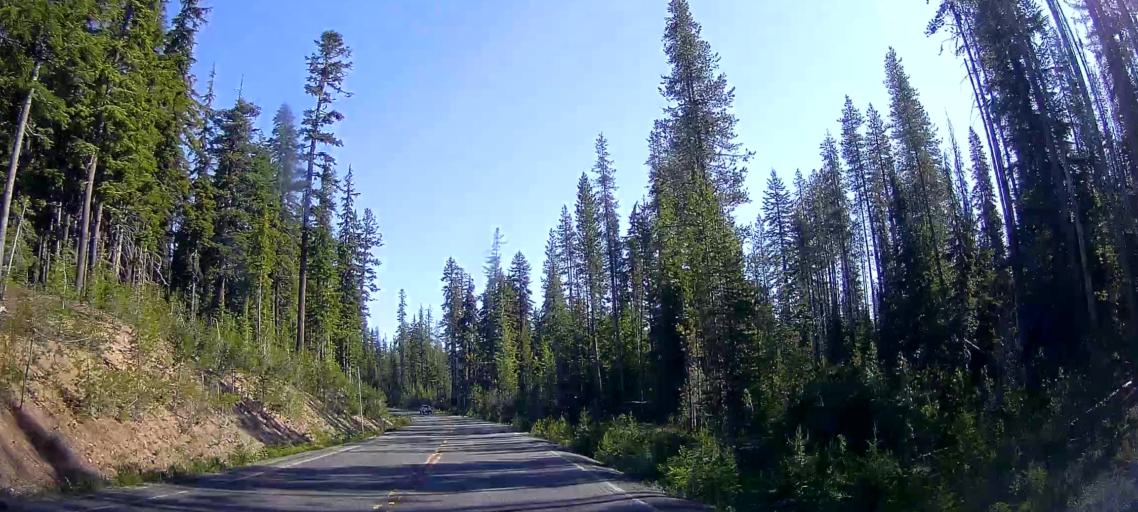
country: US
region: Oregon
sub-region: Jackson County
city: Shady Cove
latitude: 42.8457
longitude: -122.1466
